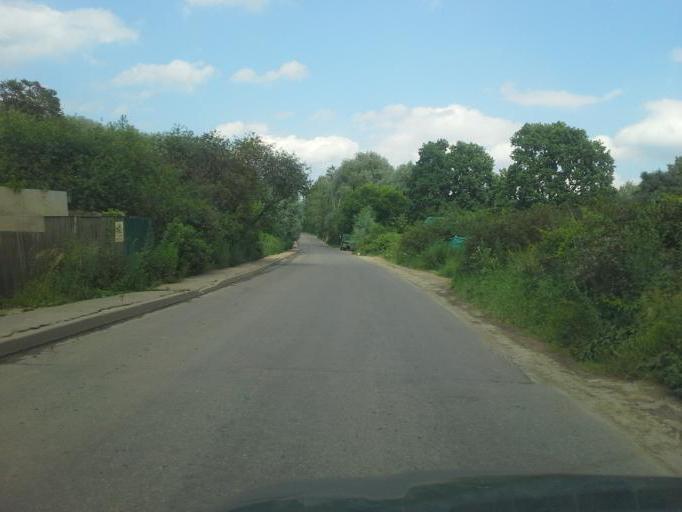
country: RU
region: Moskovskaya
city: Barvikha
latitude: 55.7205
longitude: 37.2800
